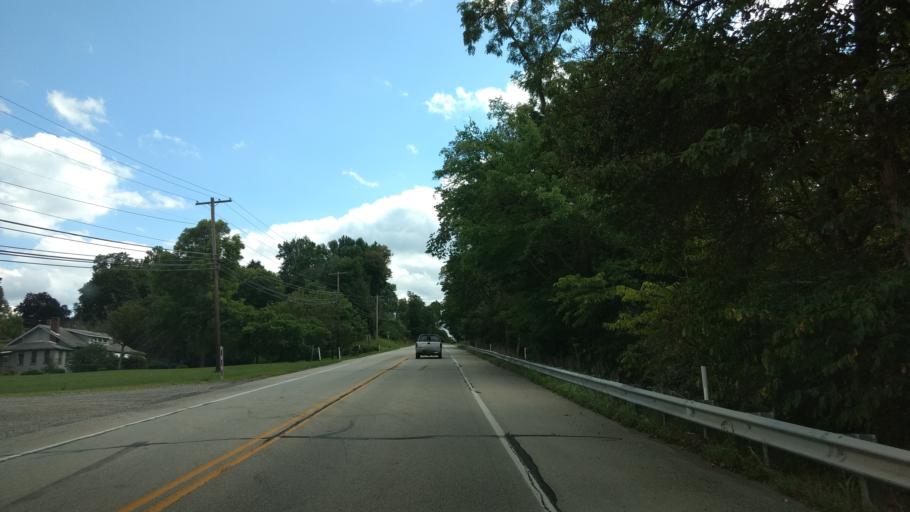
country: US
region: Pennsylvania
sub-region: Armstrong County
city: Apollo
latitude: 40.5639
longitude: -79.5799
